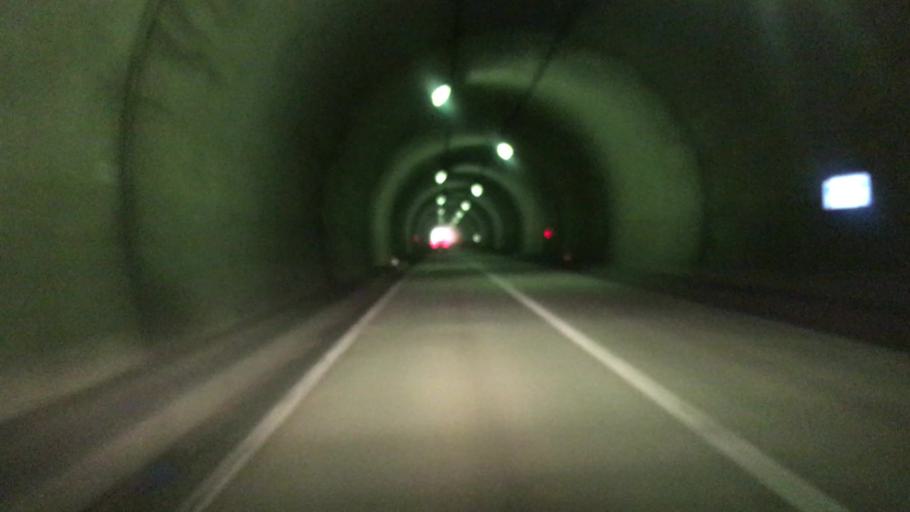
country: JP
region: Hyogo
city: Toyooka
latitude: 35.4201
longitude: 134.7413
